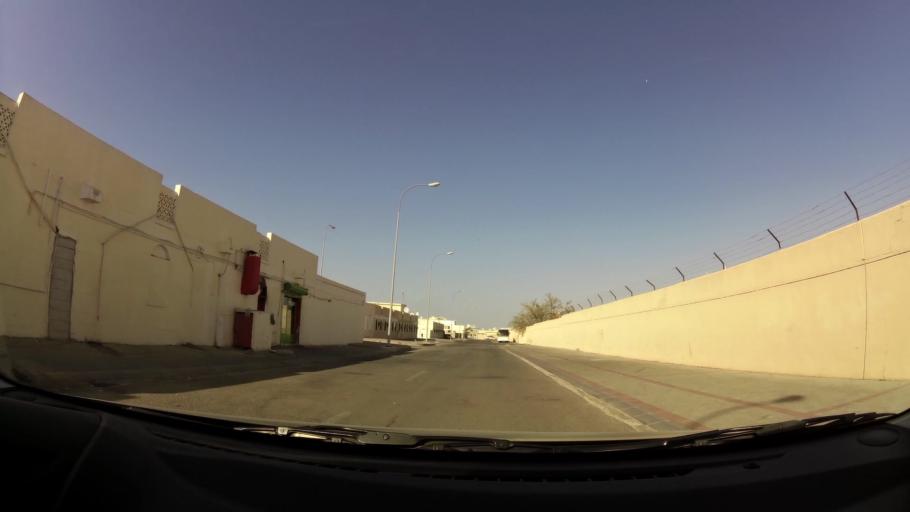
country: OM
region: Muhafazat Masqat
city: As Sib al Jadidah
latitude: 23.6204
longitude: 58.1892
